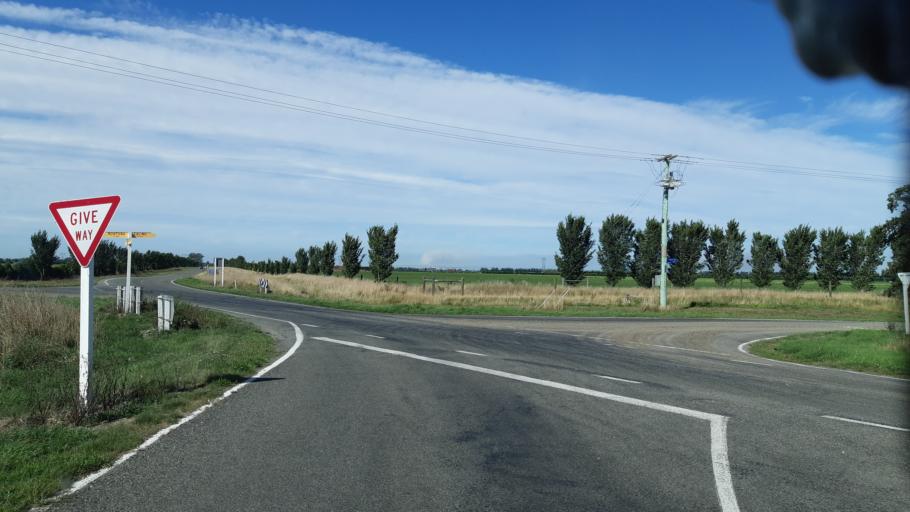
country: NZ
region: Canterbury
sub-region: Ashburton District
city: Tinwald
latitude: -43.9242
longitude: 171.4458
